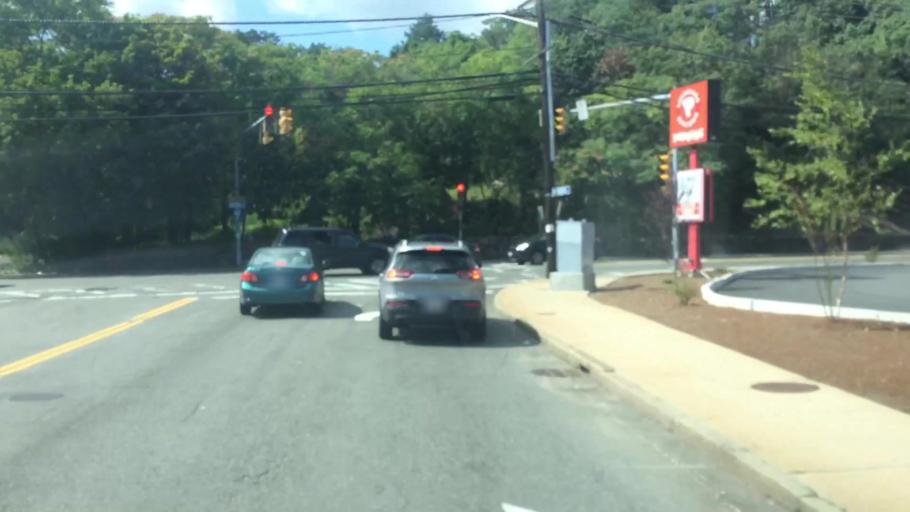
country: US
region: Massachusetts
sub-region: Essex County
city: Lynn
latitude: 42.4709
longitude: -70.9586
